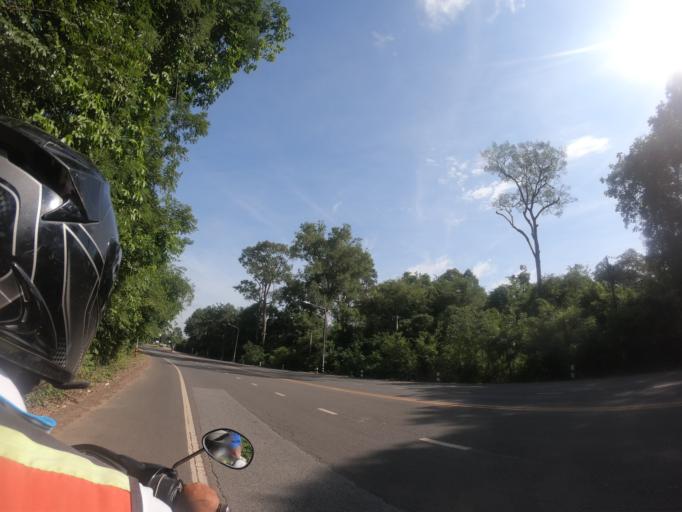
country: TH
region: Surin
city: Kap Choeng
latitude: 14.4495
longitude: 103.7000
